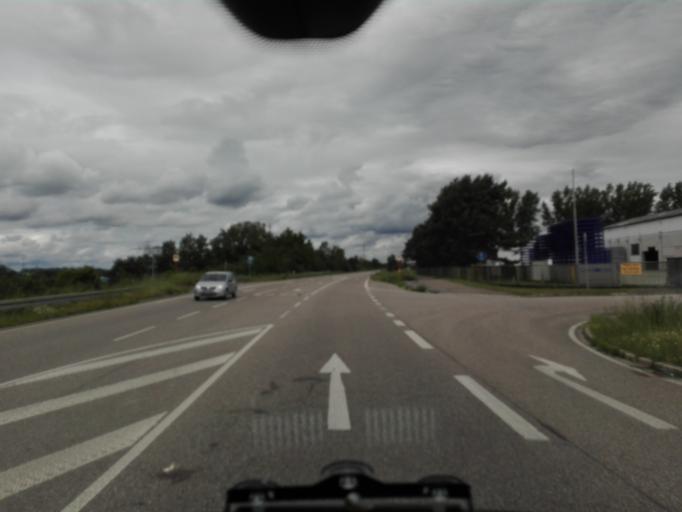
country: DE
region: Baden-Wuerttemberg
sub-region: Karlsruhe Region
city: Philippsburg
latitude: 49.2186
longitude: 8.4695
